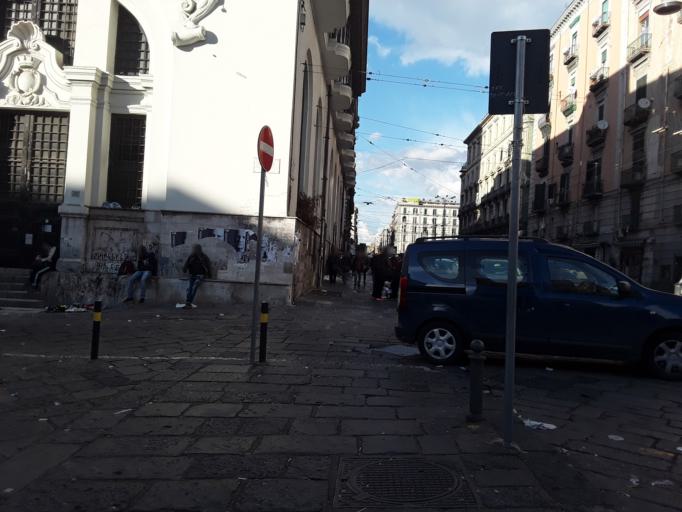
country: IT
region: Campania
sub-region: Provincia di Napoli
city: Napoli
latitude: 40.8504
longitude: 14.2684
